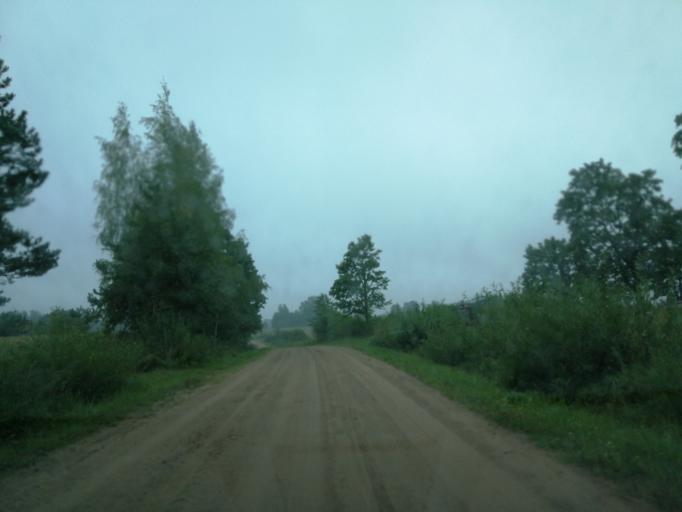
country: LV
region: Preilu Rajons
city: Jaunaglona
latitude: 56.3086
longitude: 26.9974
